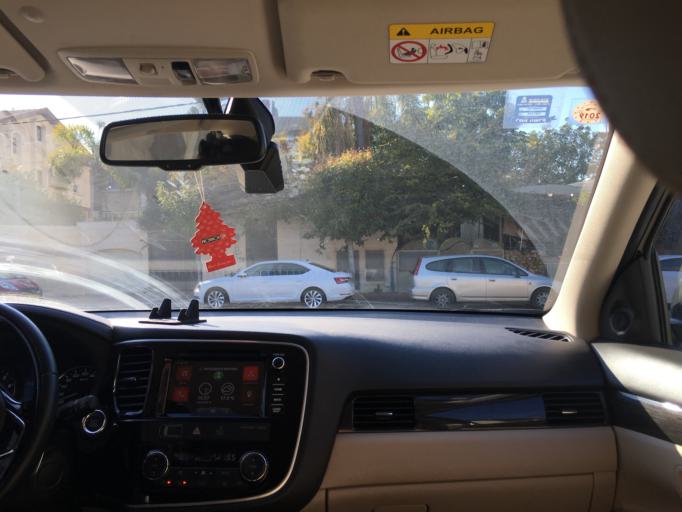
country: IL
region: Tel Aviv
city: Ramat HaSharon
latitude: 32.1520
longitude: 34.8298
